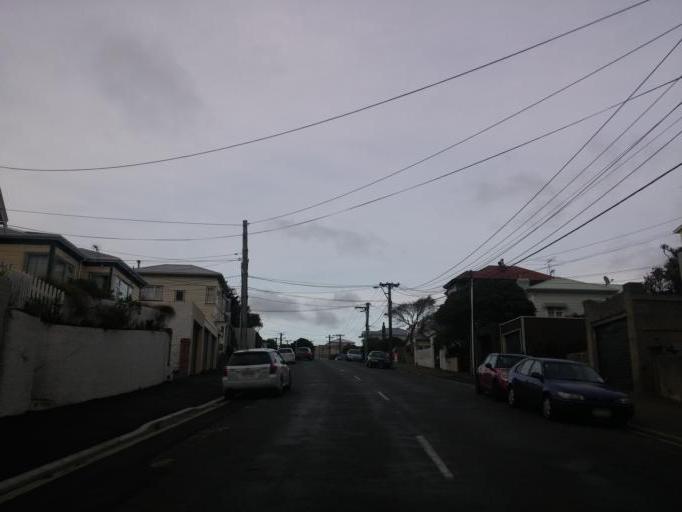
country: NZ
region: Wellington
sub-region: Wellington City
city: Wellington
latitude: -41.3039
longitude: 174.7669
